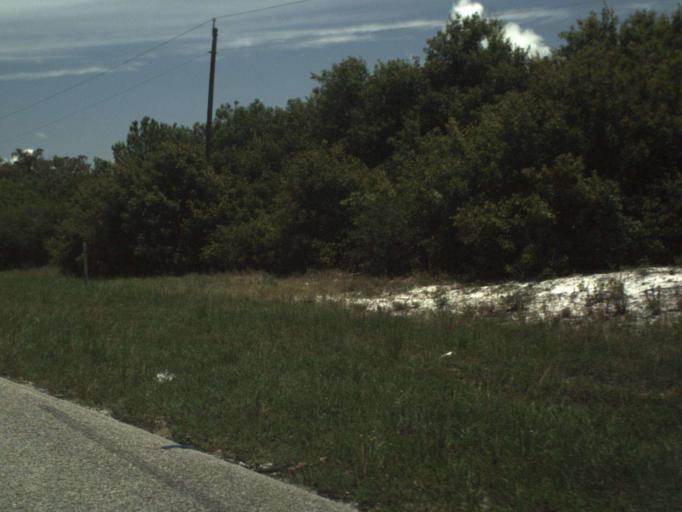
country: US
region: Florida
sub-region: Saint Lucie County
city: Lakewood Park
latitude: 27.5364
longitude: -80.3638
